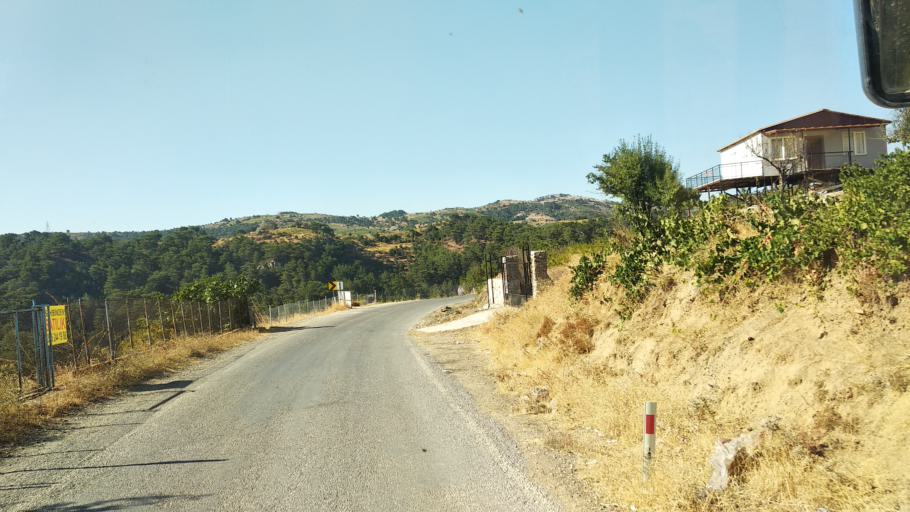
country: TR
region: Izmir
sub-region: Seferihisar
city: Seferhisar
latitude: 38.3136
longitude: 26.9549
